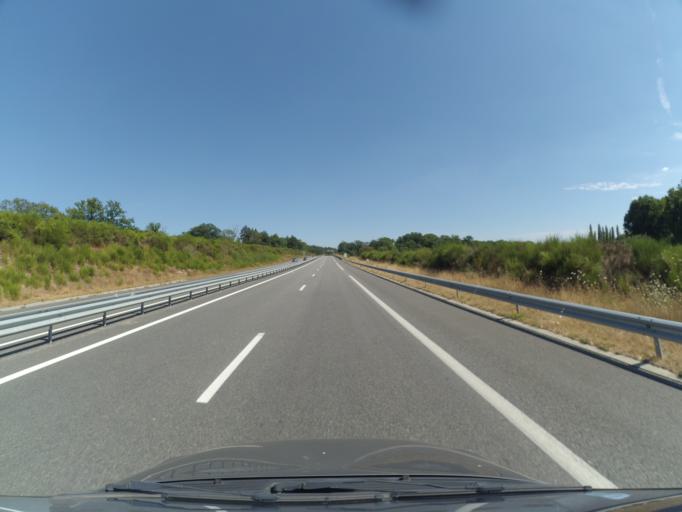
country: FR
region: Limousin
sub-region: Departement de la Haute-Vienne
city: Veyrac
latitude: 45.8767
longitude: 1.1078
